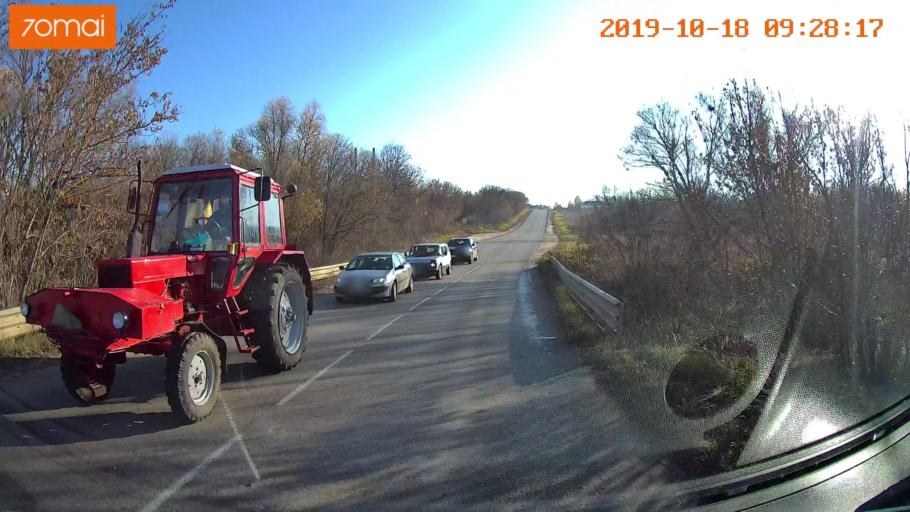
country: RU
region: Tula
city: Yefremov
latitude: 53.1341
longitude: 38.1346
